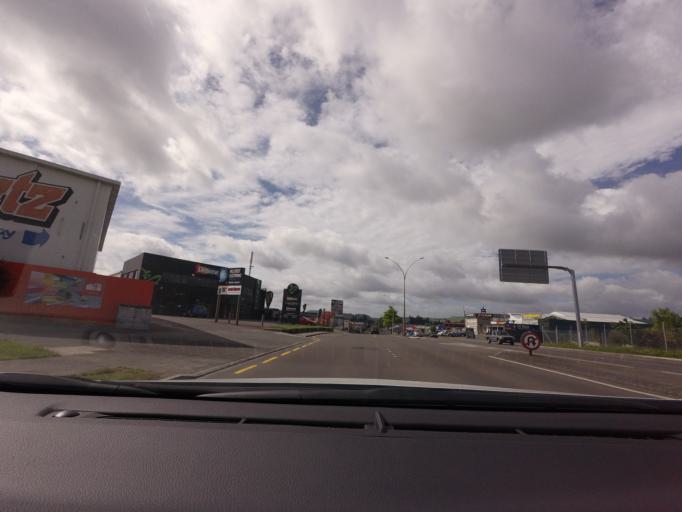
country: NZ
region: Bay of Plenty
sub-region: Rotorua District
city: Rotorua
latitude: -38.1263
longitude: 176.2321
